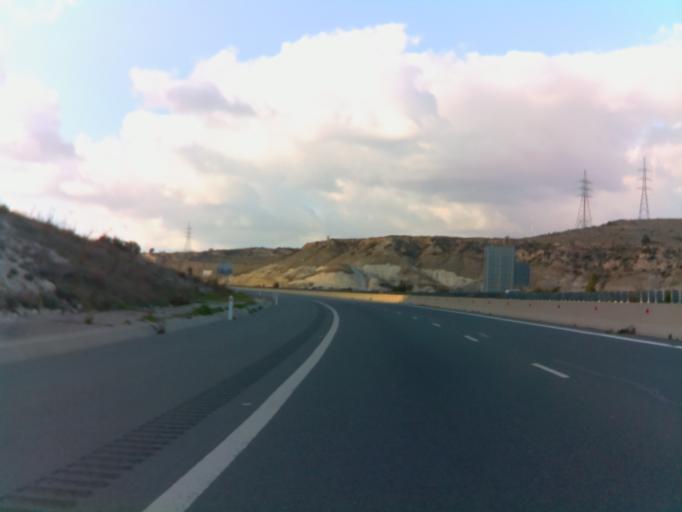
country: CY
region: Pafos
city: Mesogi
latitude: 34.7617
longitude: 32.4899
